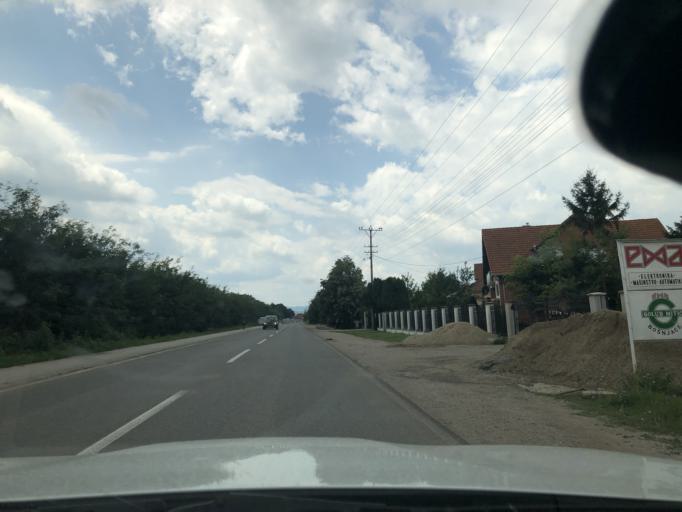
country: RS
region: Central Serbia
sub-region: Jablanicki Okrug
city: Lebane
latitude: 42.9531
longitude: 21.8312
